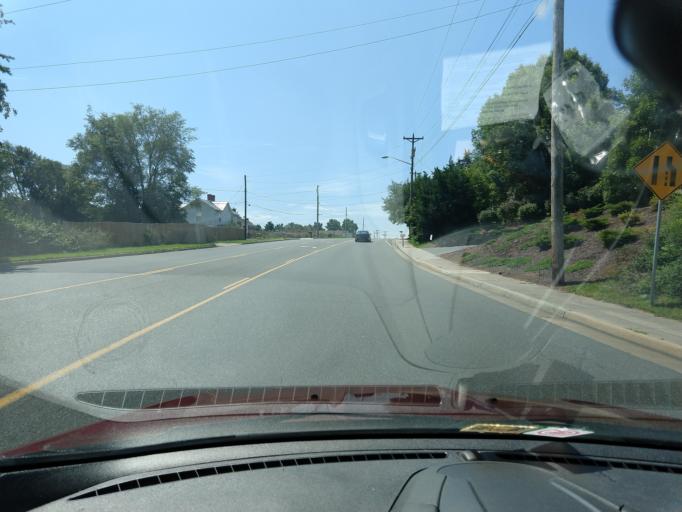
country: US
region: Virginia
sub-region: City of Harrisonburg
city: Harrisonburg
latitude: 38.4623
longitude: -78.8696
